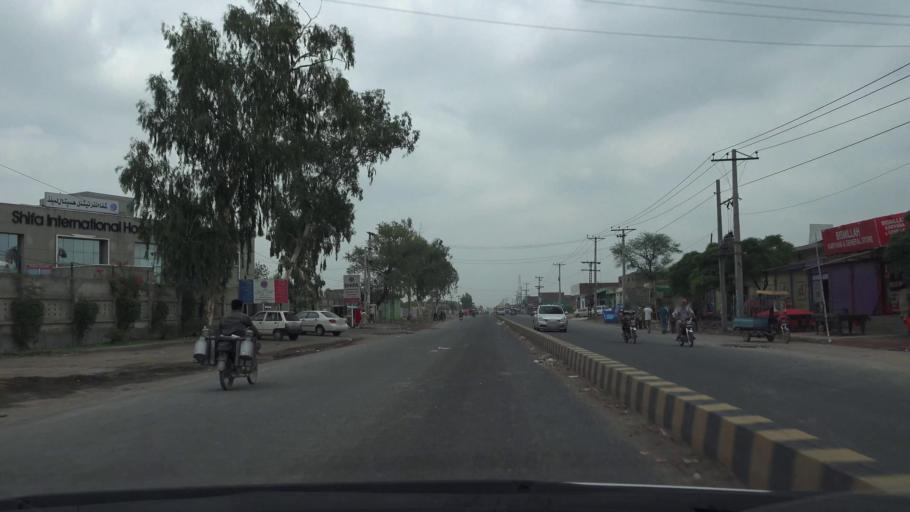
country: PK
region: Punjab
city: Faisalabad
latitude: 31.3936
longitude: 73.1790
